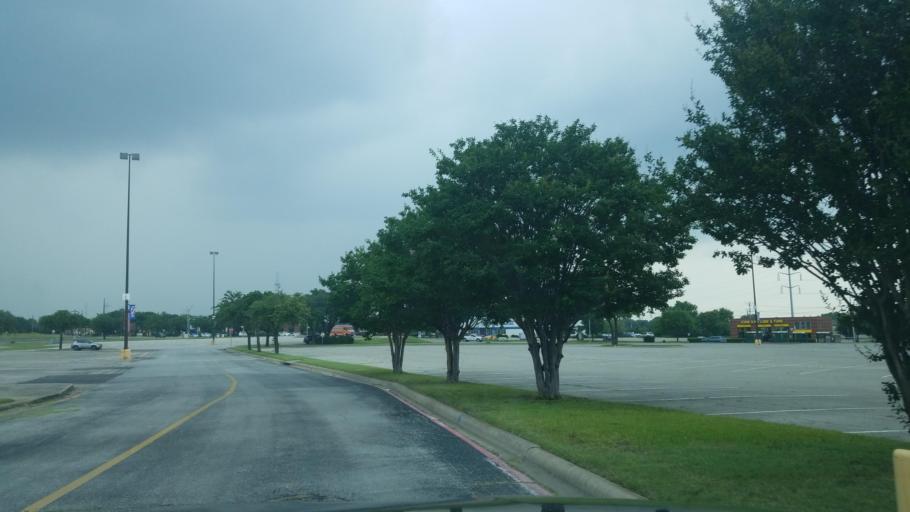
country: US
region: Texas
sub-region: Denton County
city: Denton
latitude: 33.1916
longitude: -97.1061
